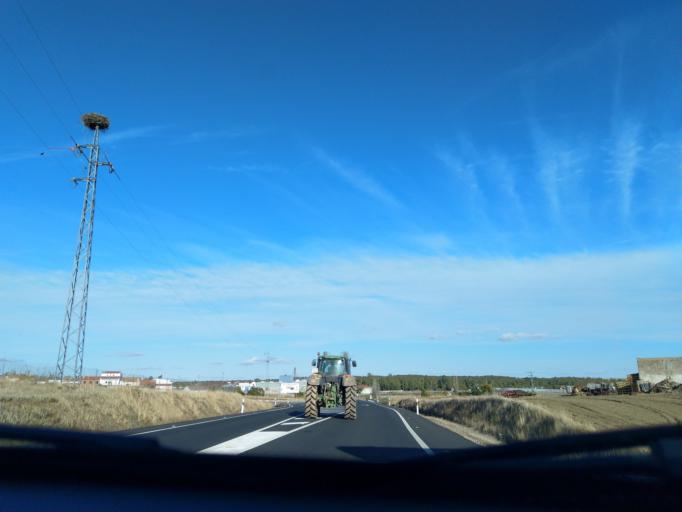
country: ES
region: Extremadura
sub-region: Provincia de Badajoz
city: Berlanga
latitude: 38.2744
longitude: -5.8302
